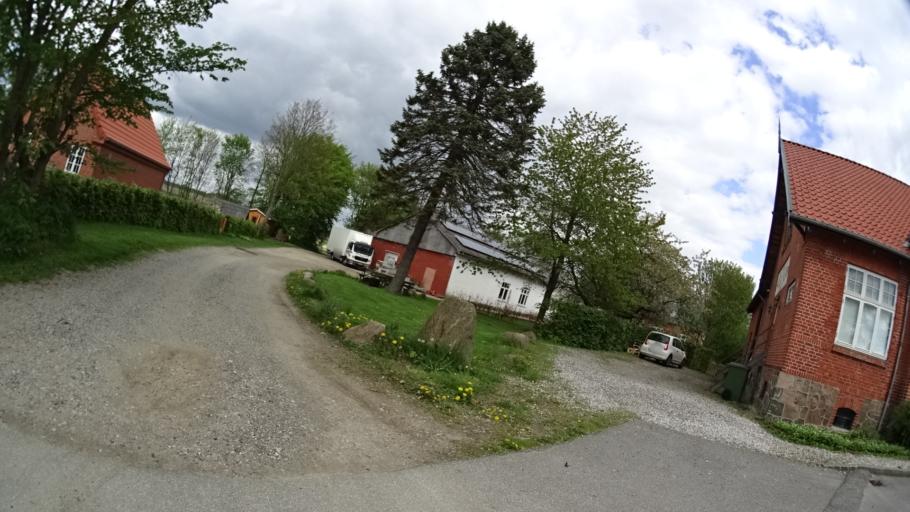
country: DK
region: Central Jutland
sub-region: Arhus Kommune
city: Kolt
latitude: 56.1307
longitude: 10.0445
